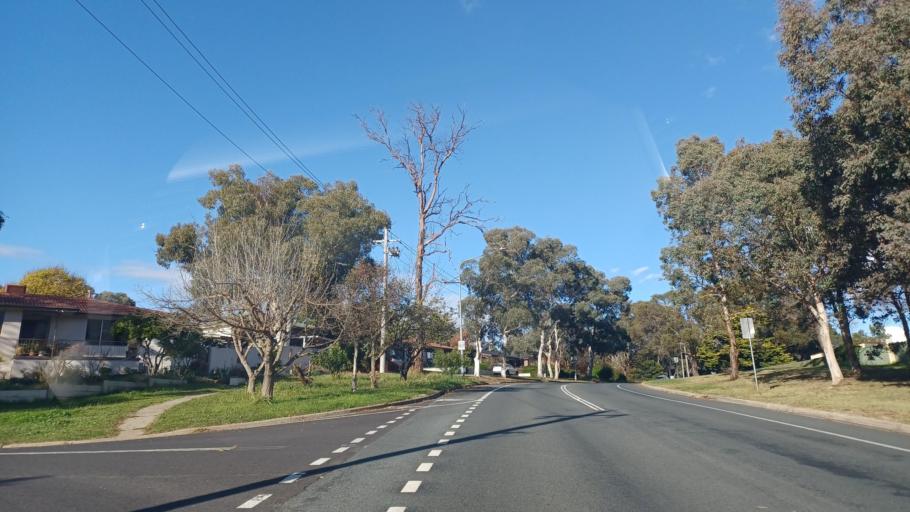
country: AU
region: Australian Capital Territory
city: Belconnen
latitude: -35.1972
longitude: 149.0434
